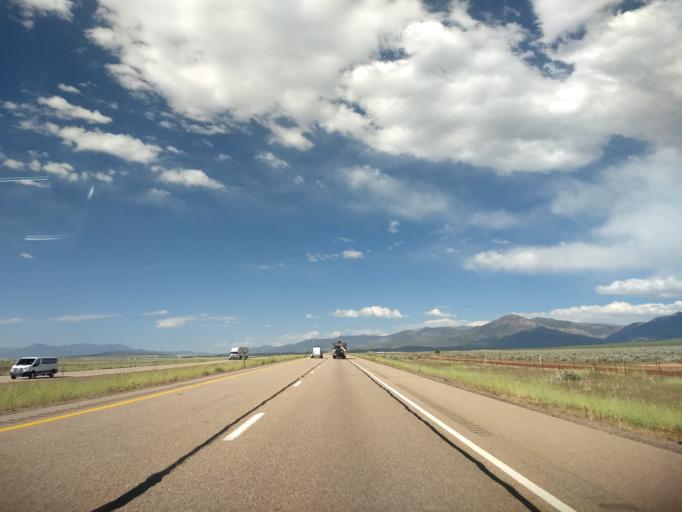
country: US
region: Utah
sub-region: Millard County
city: Fillmore
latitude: 38.9119
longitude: -112.3894
